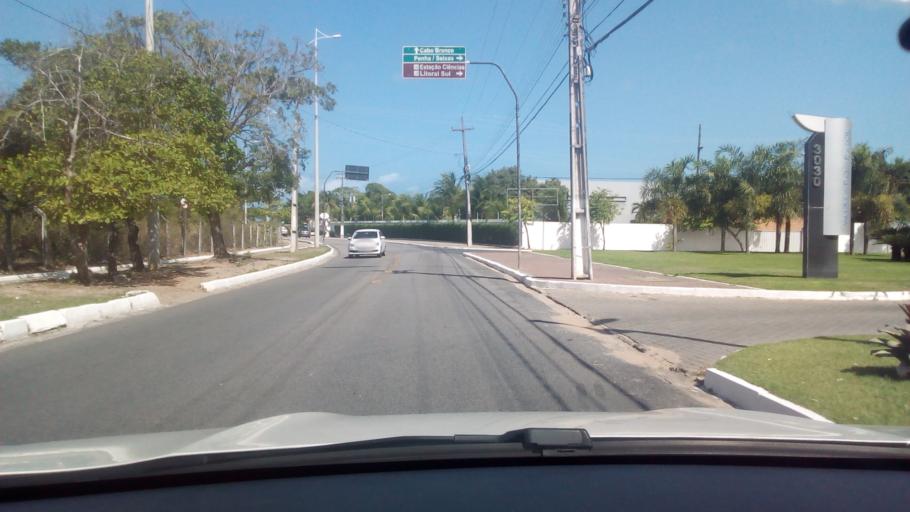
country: BR
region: Paraiba
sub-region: Joao Pessoa
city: Joao Pessoa
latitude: -7.1469
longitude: -34.8101
